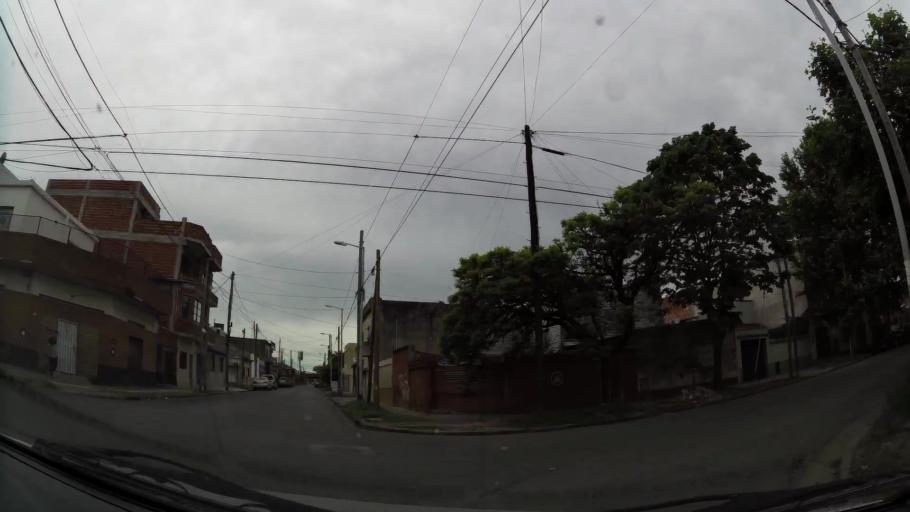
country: AR
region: Buenos Aires
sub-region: Partido de Avellaneda
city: Avellaneda
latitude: -34.6621
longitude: -58.3523
